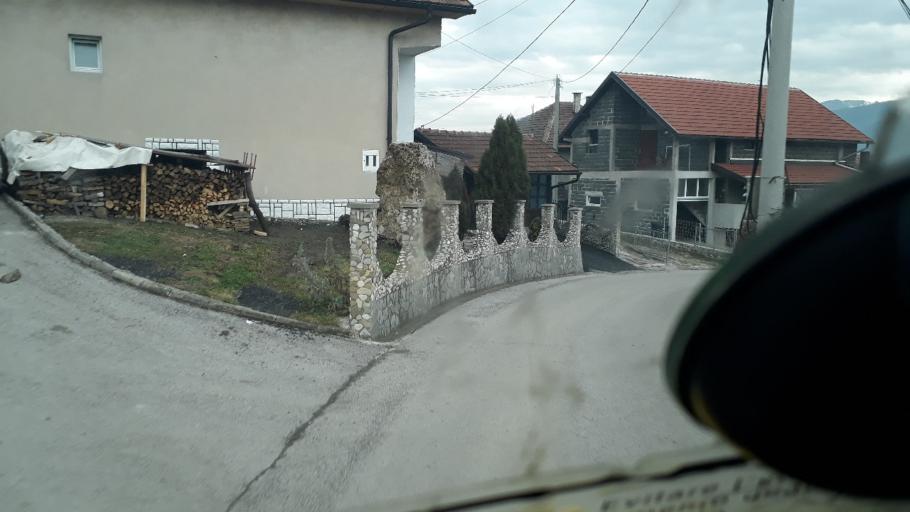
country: BA
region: Federation of Bosnia and Herzegovina
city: Zenica
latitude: 44.1918
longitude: 17.9513
